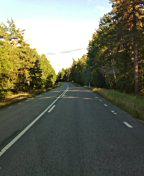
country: SE
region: Uppsala
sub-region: Habo Kommun
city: Balsta
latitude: 59.6444
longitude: 17.4342
